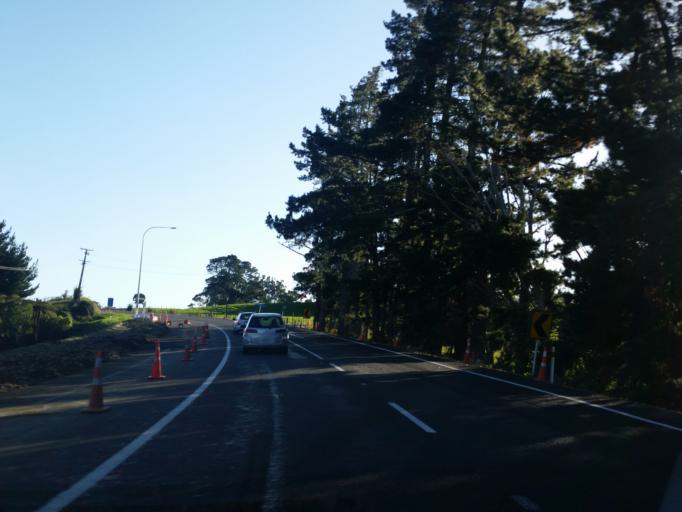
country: NZ
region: Bay of Plenty
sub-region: Western Bay of Plenty District
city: Waihi Beach
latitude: -37.4644
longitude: 175.9370
